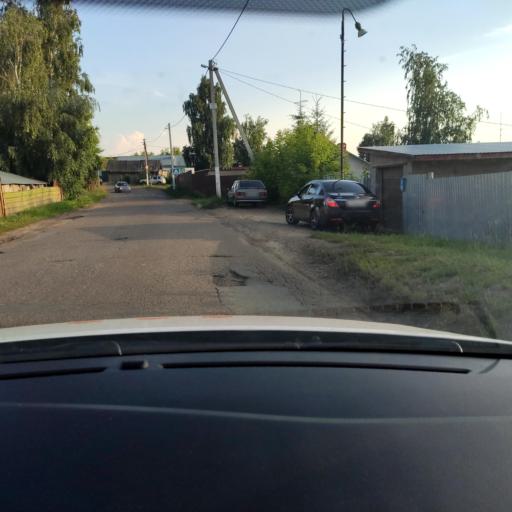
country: RU
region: Tatarstan
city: Vysokaya Gora
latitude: 55.9768
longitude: 49.3064
